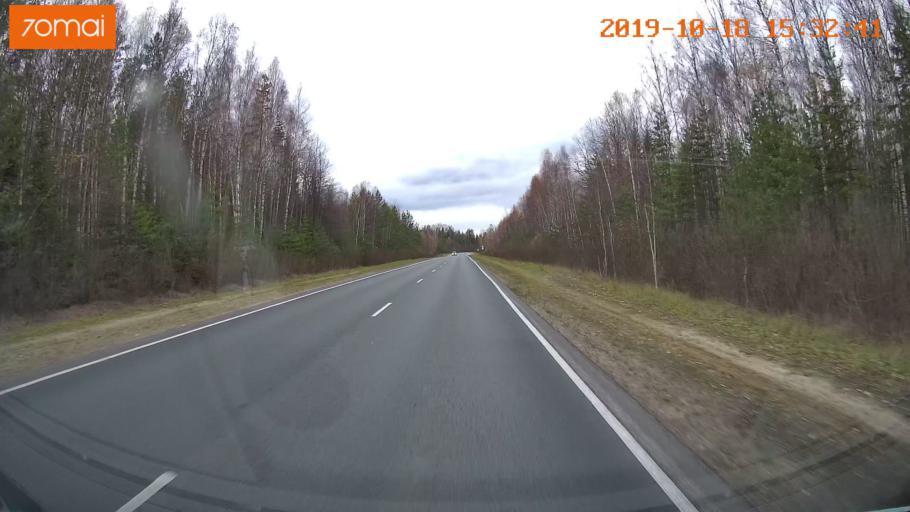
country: RU
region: Vladimir
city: Anopino
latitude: 55.8296
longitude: 40.6491
